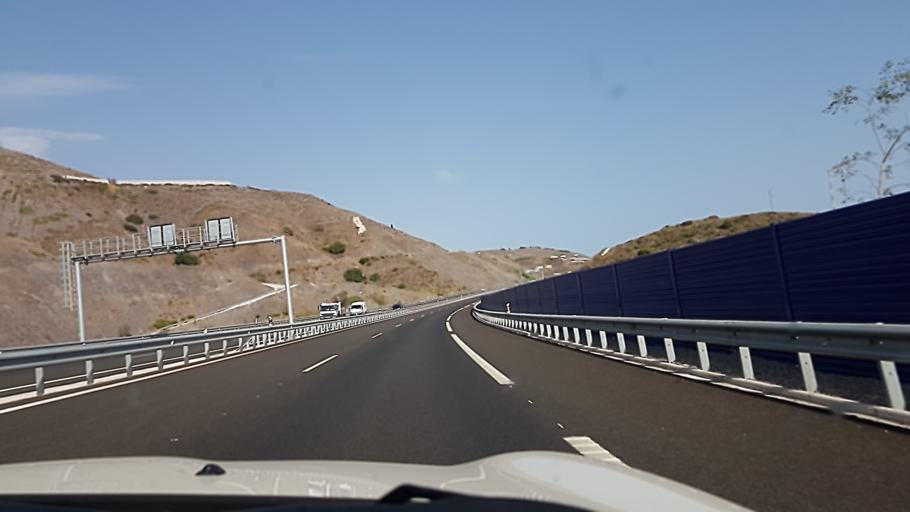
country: ES
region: Andalusia
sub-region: Provincia de Granada
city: Sorvilan
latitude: 36.7573
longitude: -3.2390
